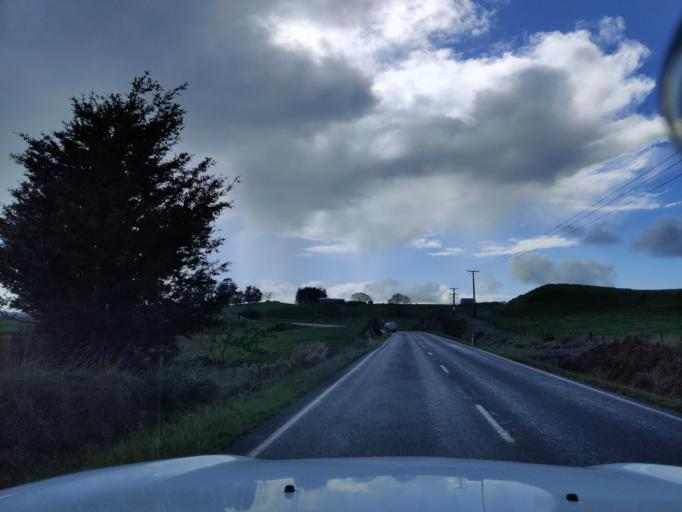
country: NZ
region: Waikato
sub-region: Waikato District
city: Ngaruawahia
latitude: -37.5896
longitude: 175.2123
